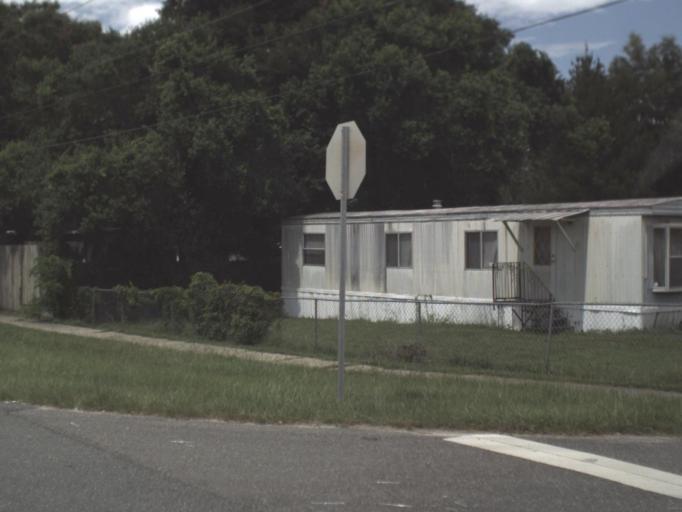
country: US
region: Florida
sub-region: Citrus County
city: Hernando
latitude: 28.9313
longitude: -82.3770
